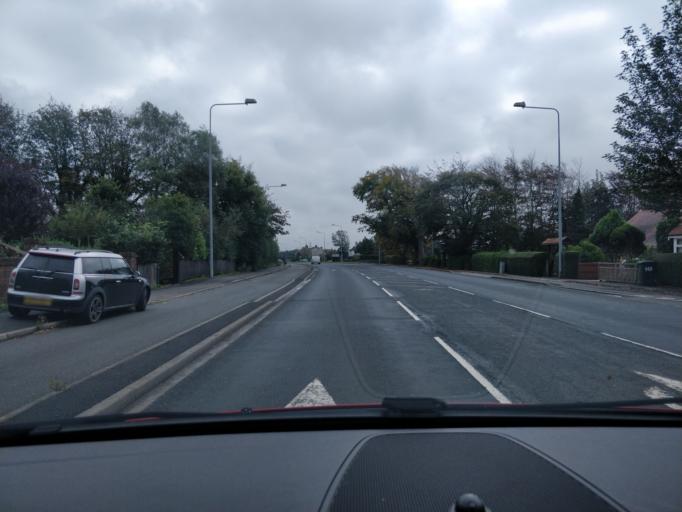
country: GB
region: England
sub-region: Sefton
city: Southport
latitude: 53.6253
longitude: -2.9626
